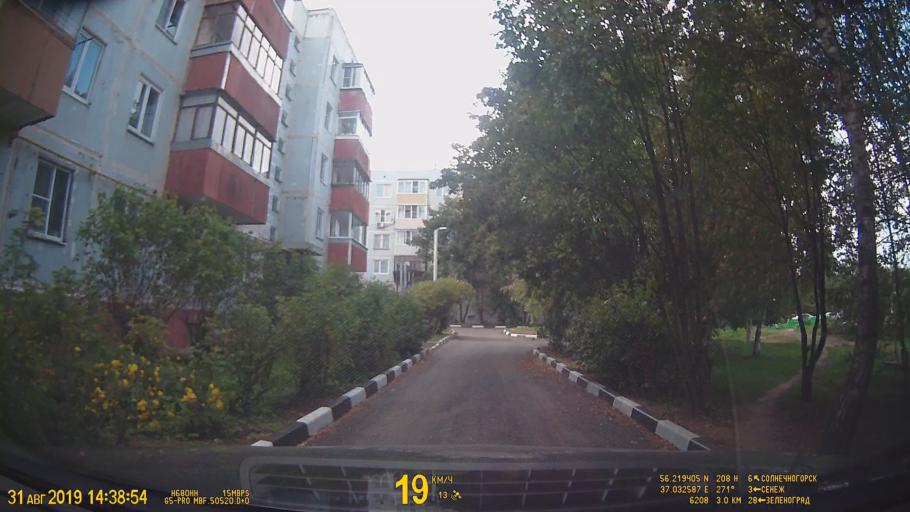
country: RU
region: Moskovskaya
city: Solnechnogorsk
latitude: 56.2194
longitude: 37.0324
